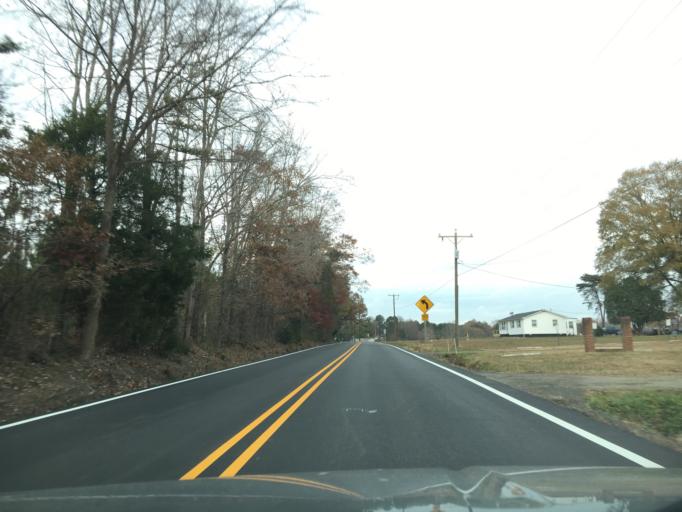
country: US
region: Virginia
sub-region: Cumberland County
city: Cumberland
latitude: 37.4648
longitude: -78.2805
